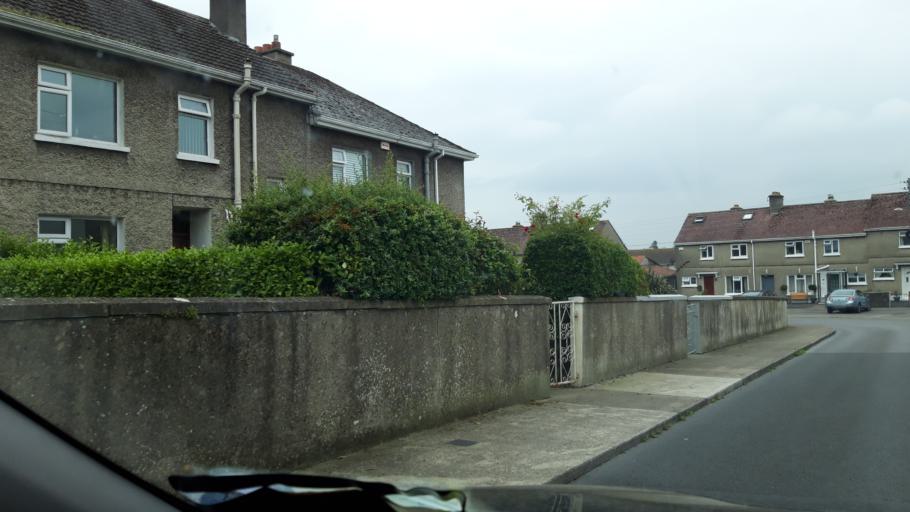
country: IE
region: Munster
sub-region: South Tipperary
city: Cluain Meala
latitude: 52.3601
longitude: -7.6927
